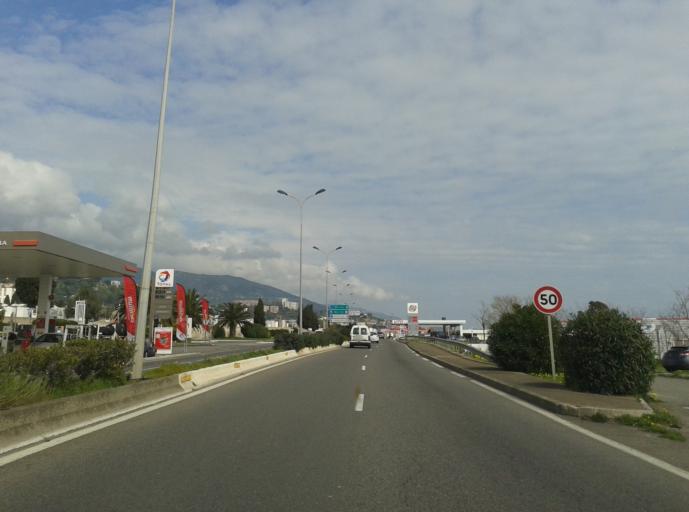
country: FR
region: Corsica
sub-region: Departement de la Haute-Corse
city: Bastia
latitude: 42.6736
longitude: 9.4439
